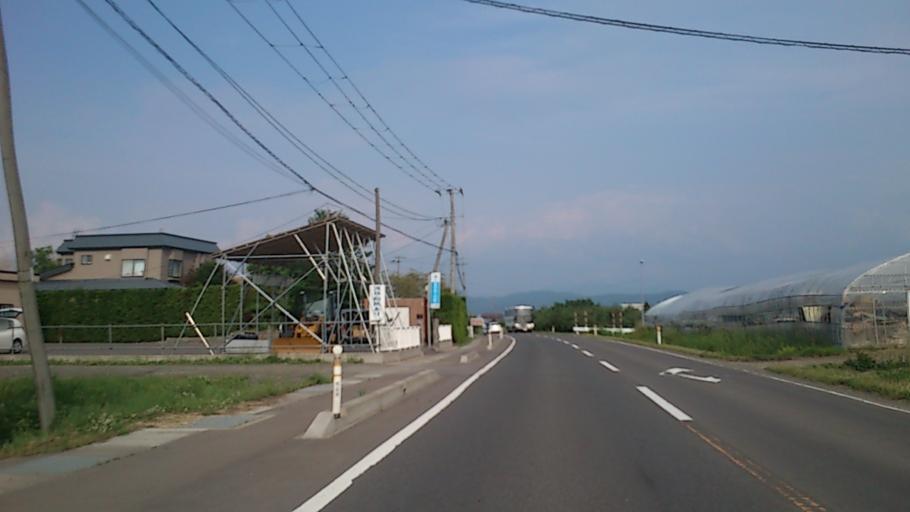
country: JP
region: Aomori
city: Hirosaki
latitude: 40.5590
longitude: 140.4986
